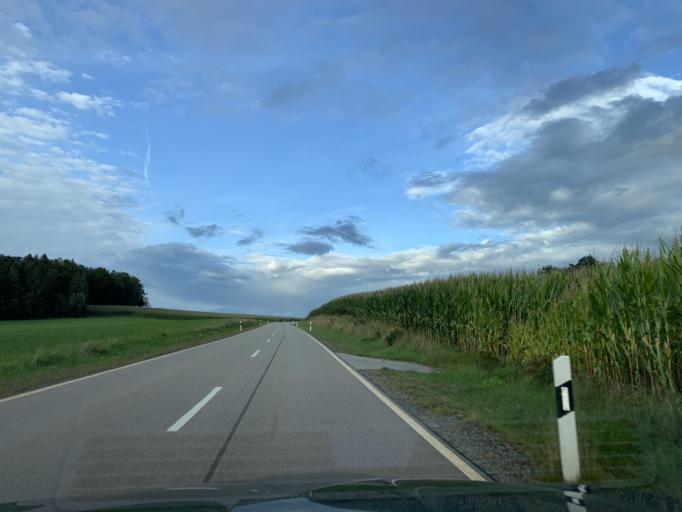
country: DE
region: Bavaria
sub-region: Upper Palatinate
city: Thanstein
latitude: 49.4017
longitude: 12.4461
